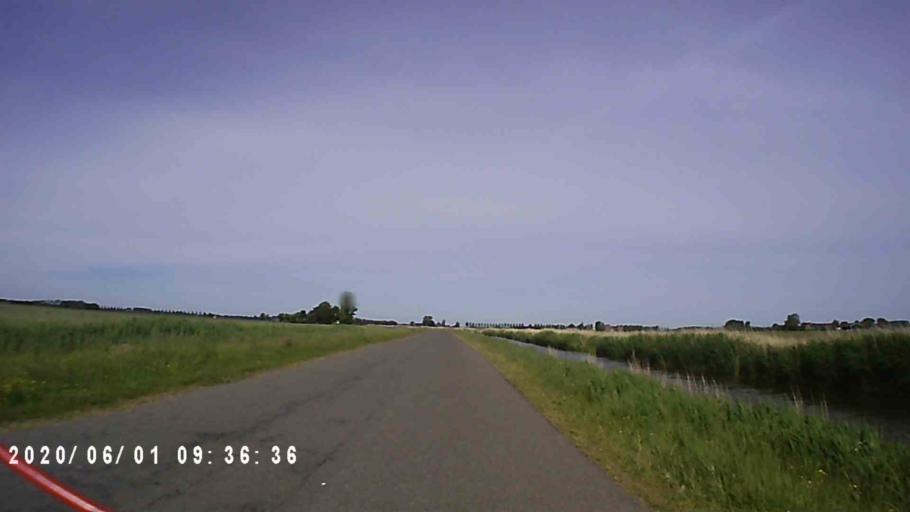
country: NL
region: Friesland
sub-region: Gemeente Het Bildt
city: Sint Annaparochie
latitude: 53.2605
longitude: 5.6983
